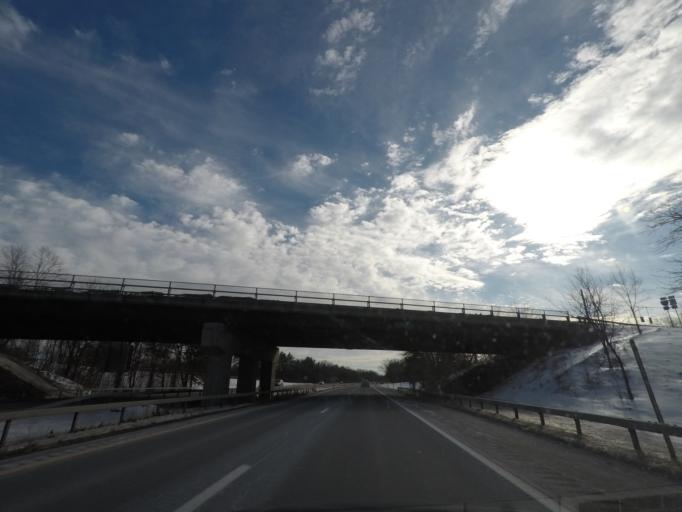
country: US
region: New York
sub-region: Schenectady County
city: Schenectady
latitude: 42.7714
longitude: -73.9267
